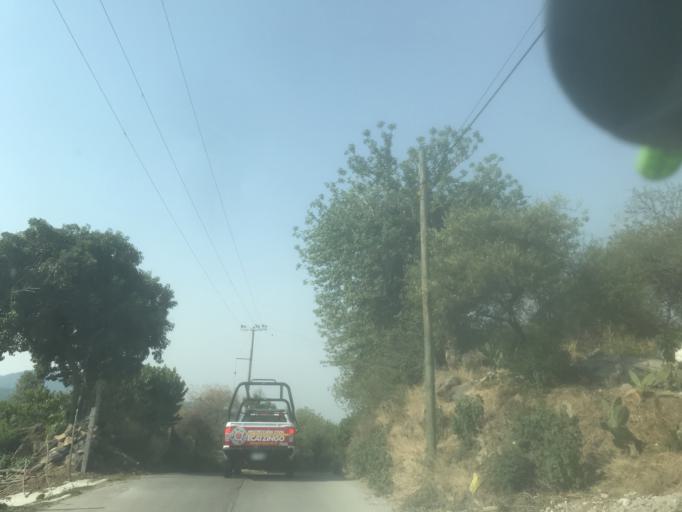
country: MX
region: Mexico
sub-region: Ecatzingo
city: San Juan Tlacotompa (Tlacotompa)
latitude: 18.9386
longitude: -98.7937
